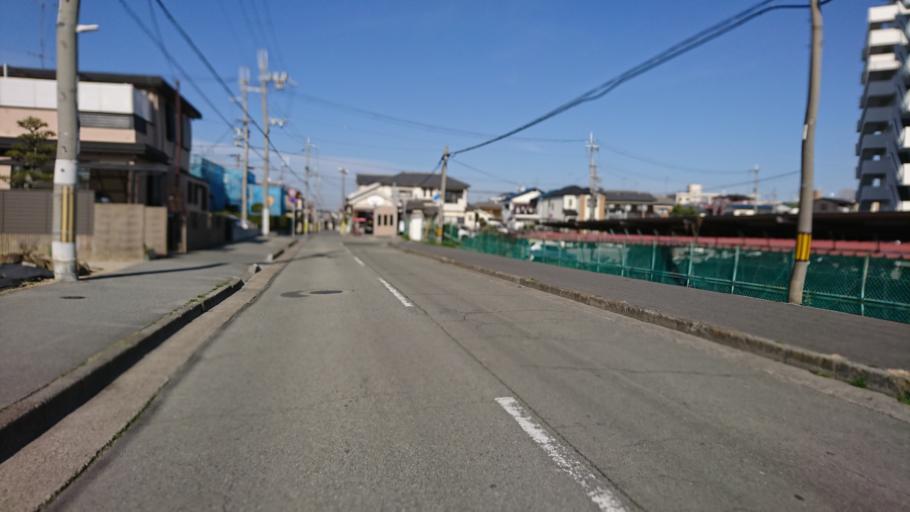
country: JP
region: Hyogo
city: Kakogawacho-honmachi
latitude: 34.7370
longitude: 134.8687
